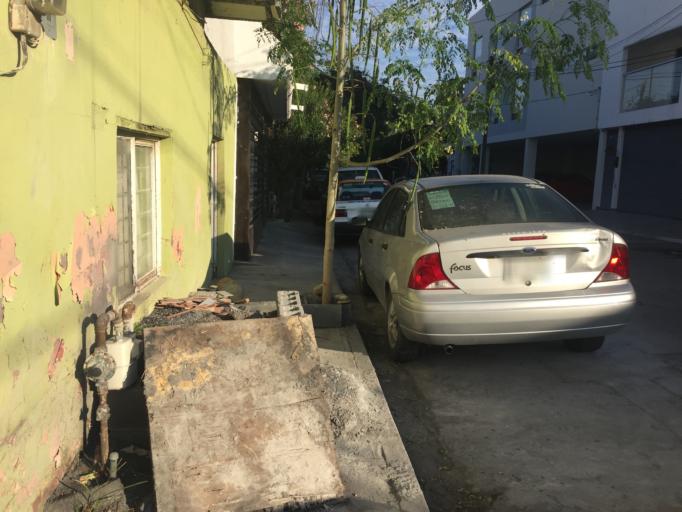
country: MX
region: Nuevo Leon
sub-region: San Pedro Garza Garcia
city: San Pedro Garza Garcia
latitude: 25.6598
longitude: -100.4035
